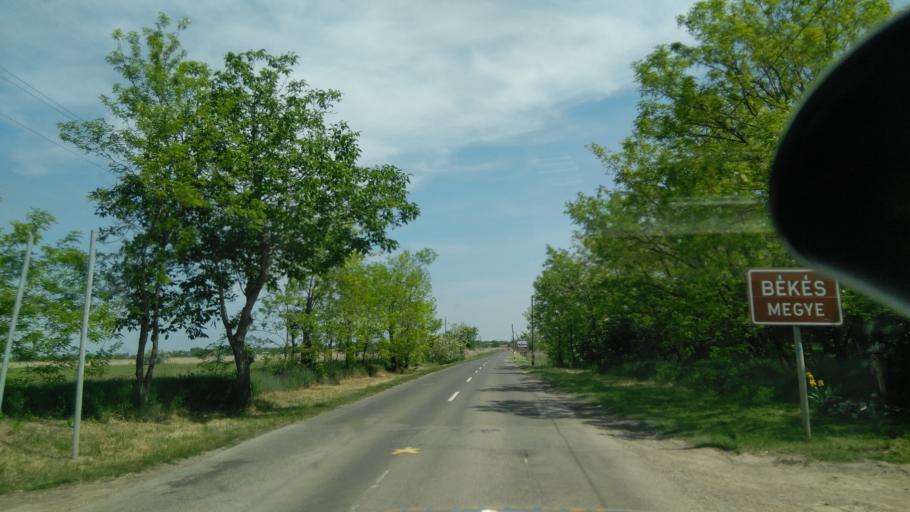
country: HU
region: Csongrad
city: Szekkutas
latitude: 46.5682
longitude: 20.5789
